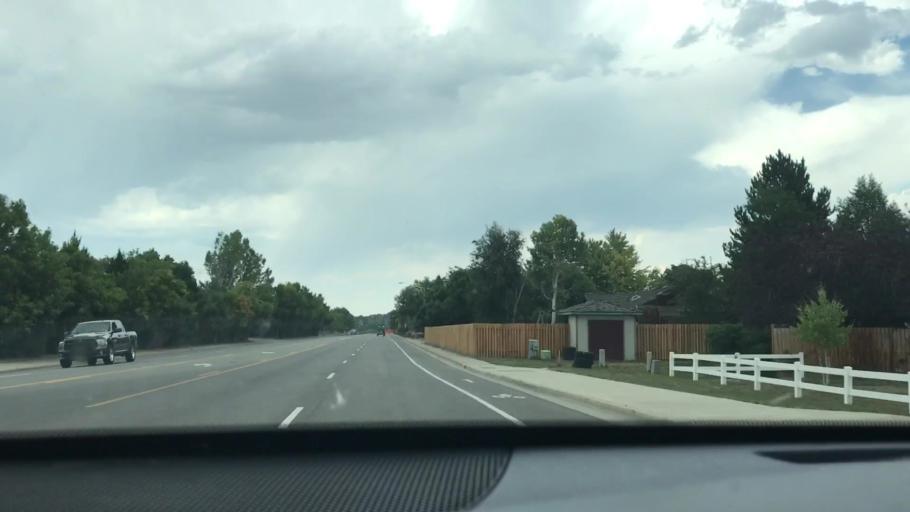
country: US
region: Colorado
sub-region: Larimer County
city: Loveland
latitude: 40.3866
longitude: -105.1159
